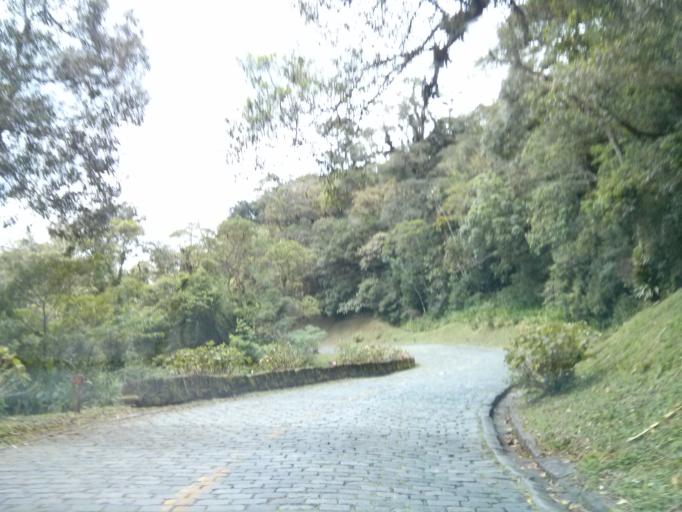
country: BR
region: Parana
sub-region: Campina Grande Do Sul
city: Campina Grande do Sul
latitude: -25.3494
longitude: -48.8885
